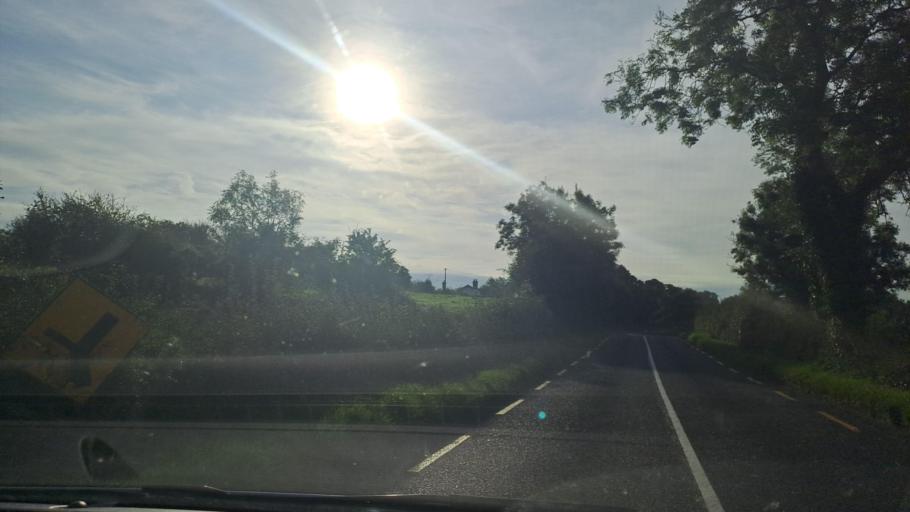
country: IE
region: Ulster
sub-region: An Cabhan
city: Kingscourt
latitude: 53.9338
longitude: -6.8195
